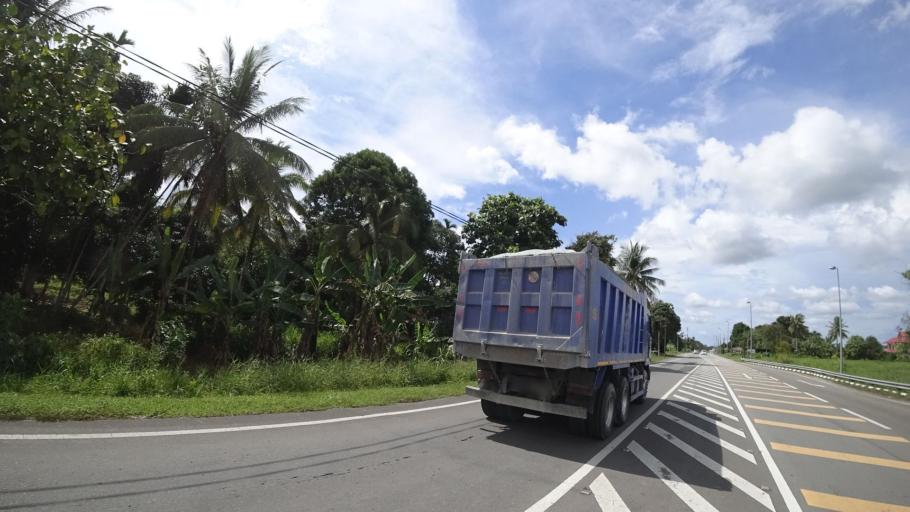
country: BN
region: Tutong
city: Tutong
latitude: 4.7510
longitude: 114.8170
